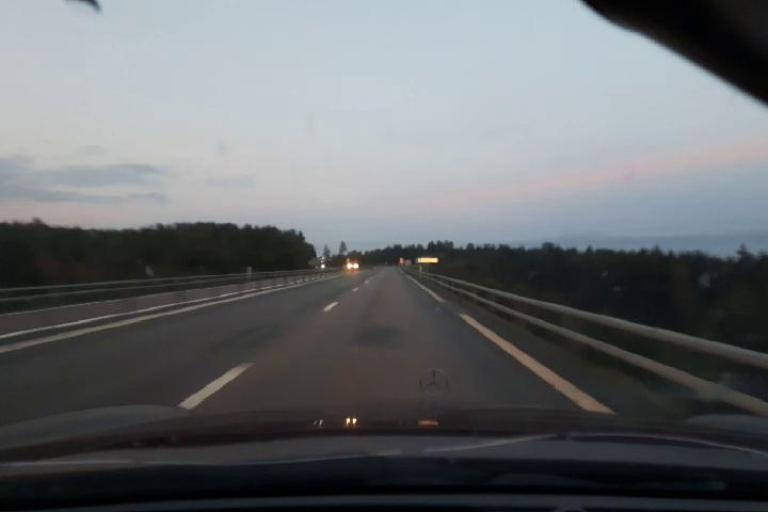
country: SE
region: Vaesternorrland
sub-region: Kramfors Kommun
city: Nordingra
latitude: 62.8789
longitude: 18.0776
